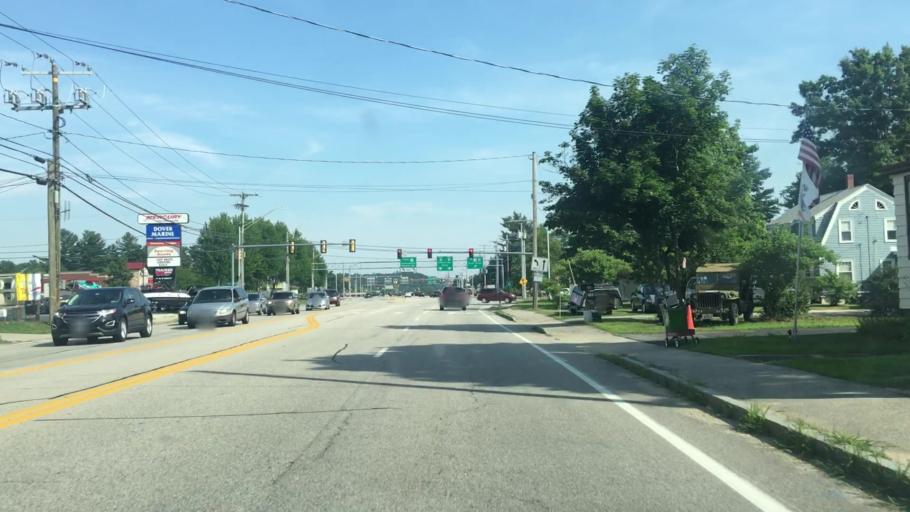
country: US
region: New Hampshire
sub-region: Strafford County
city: Dover
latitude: 43.2244
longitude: -70.8908
